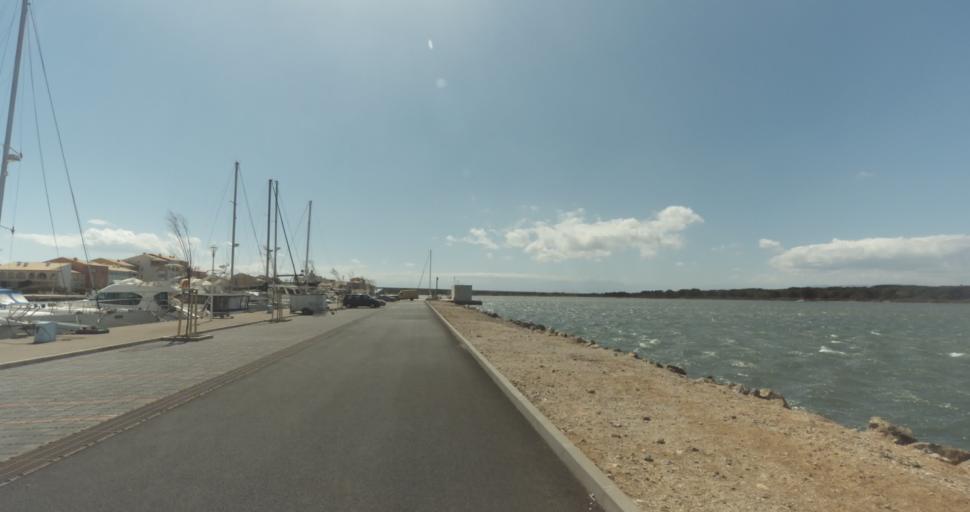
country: FR
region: Languedoc-Roussillon
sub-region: Departement de l'Aude
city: Leucate
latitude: 42.8661
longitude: 3.0386
